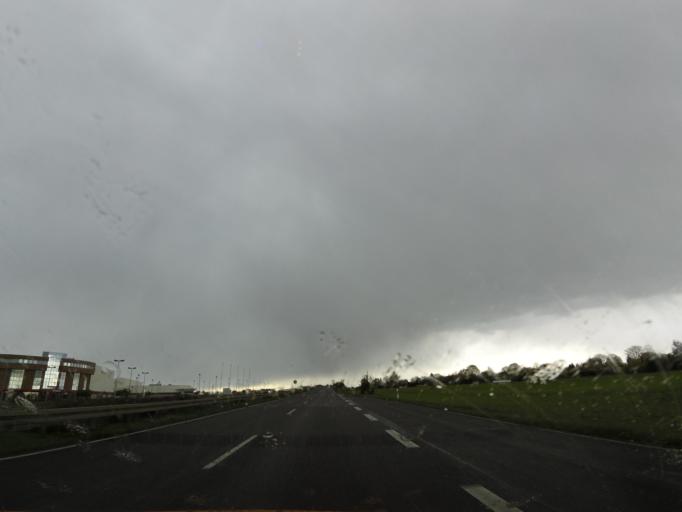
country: DE
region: Saxony-Anhalt
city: Hohendodeleben
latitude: 52.0397
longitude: 11.5186
